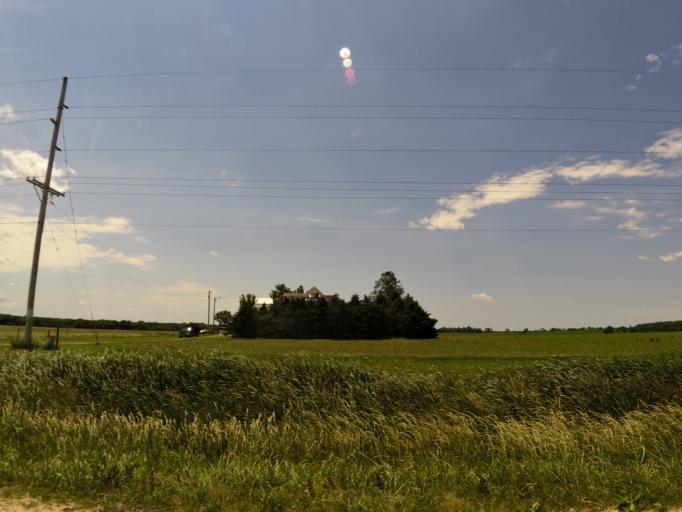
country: US
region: Iowa
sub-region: Bremer County
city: Tripoli
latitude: 42.7148
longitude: -92.1851
